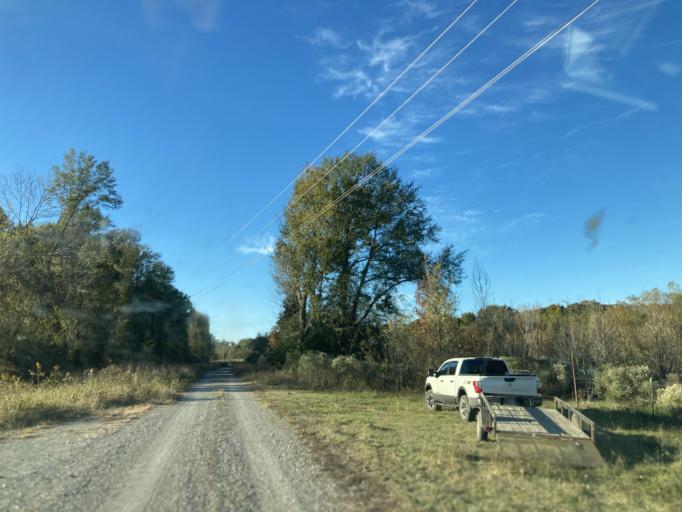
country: US
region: Mississippi
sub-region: Yazoo County
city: Yazoo City
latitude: 32.8923
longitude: -90.4315
